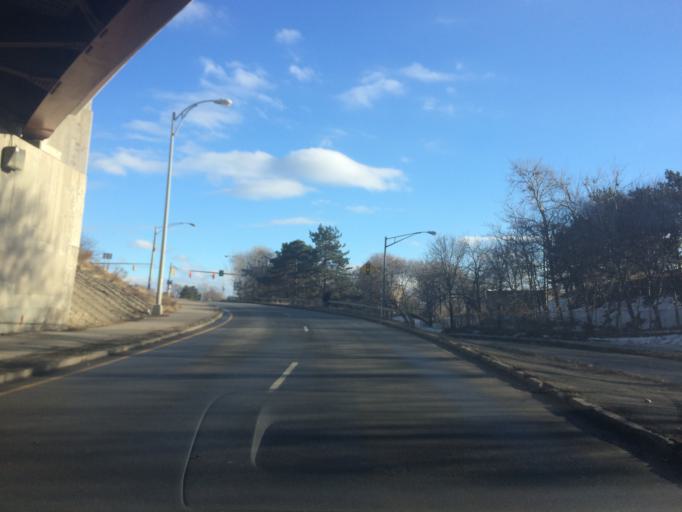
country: US
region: New York
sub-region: Monroe County
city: Rochester
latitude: 43.1508
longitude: -77.6072
